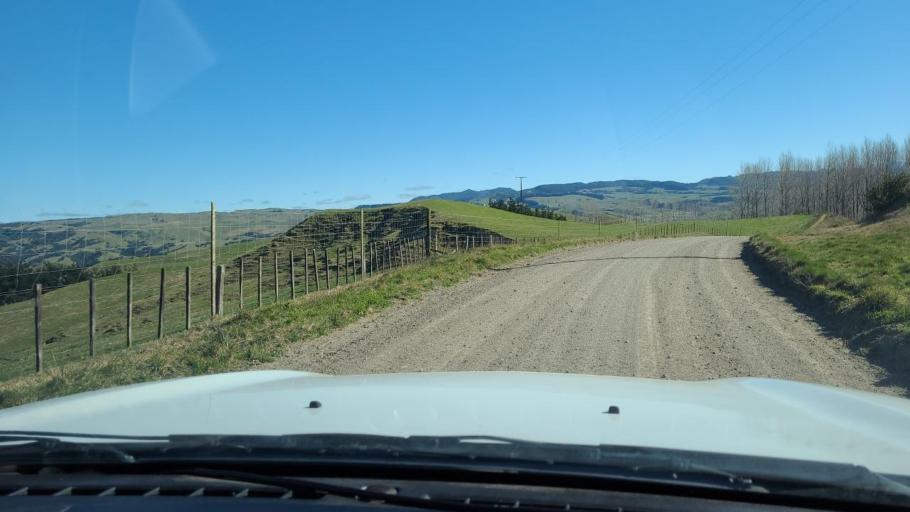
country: NZ
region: Hawke's Bay
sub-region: Napier City
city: Taradale
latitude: -39.4933
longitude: 176.4820
